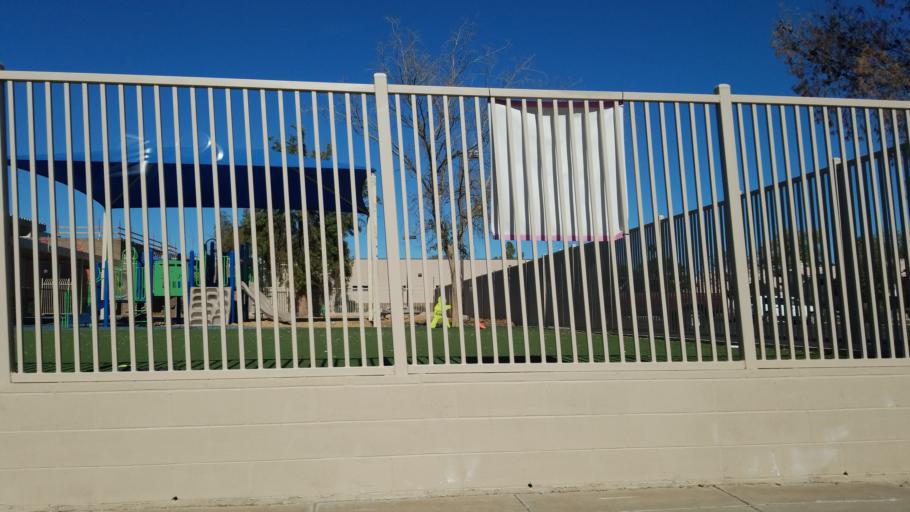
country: US
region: Arizona
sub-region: Maricopa County
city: Paradise Valley
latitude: 33.6150
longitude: -111.9349
